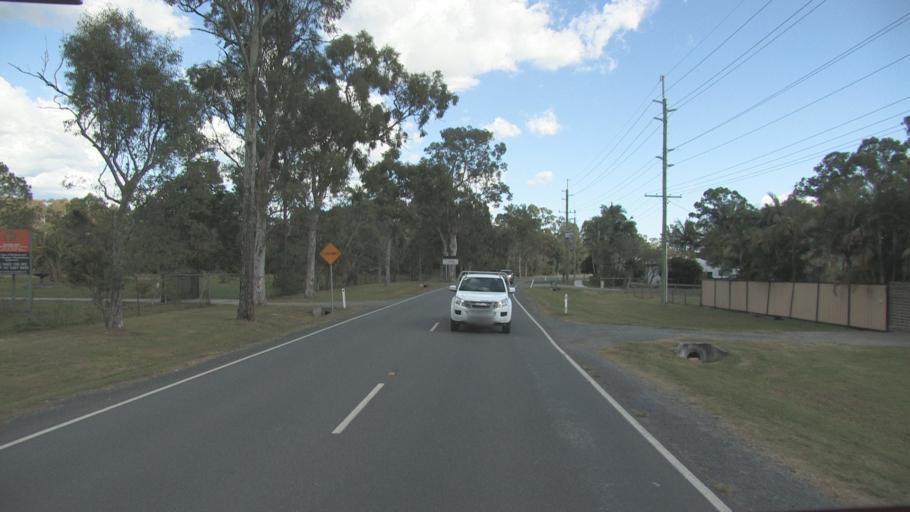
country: AU
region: Queensland
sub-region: Logan
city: Beenleigh
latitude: -27.6612
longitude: 153.2169
